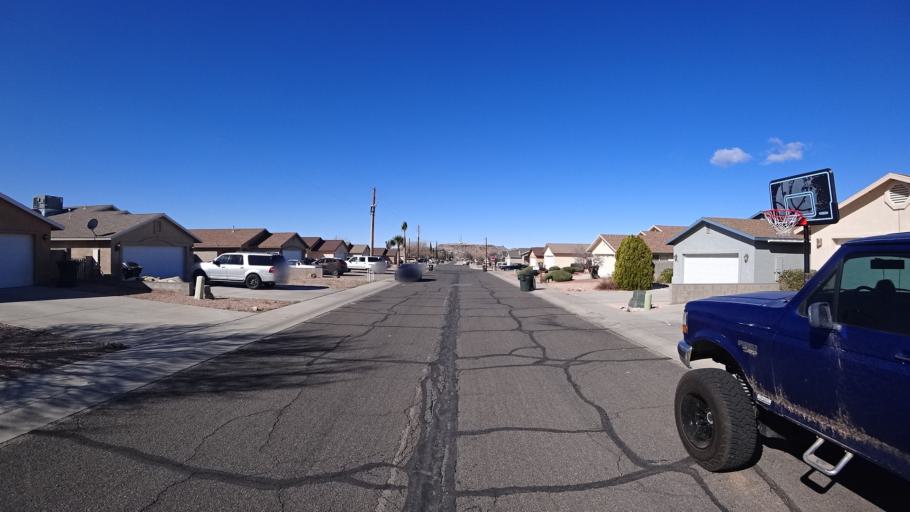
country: US
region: Arizona
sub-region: Mohave County
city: Kingman
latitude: 35.1973
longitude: -114.0149
